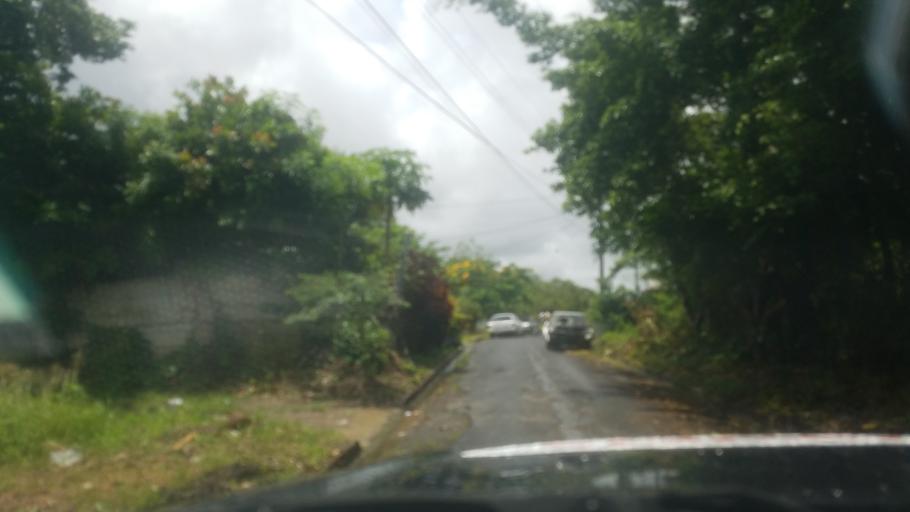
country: LC
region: Laborie Quarter
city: Laborie
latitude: 13.7527
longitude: -60.9776
